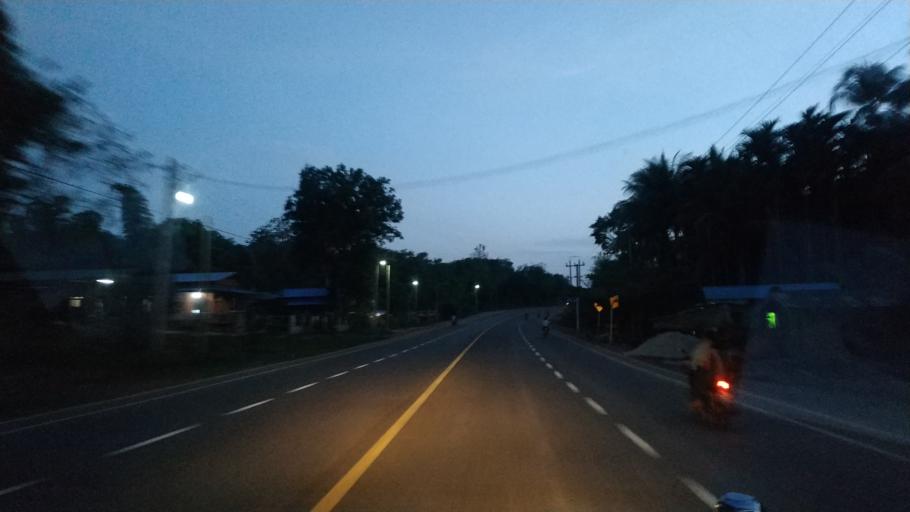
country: MM
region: Mon
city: Kyaikto
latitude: 17.3647
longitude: 97.0474
